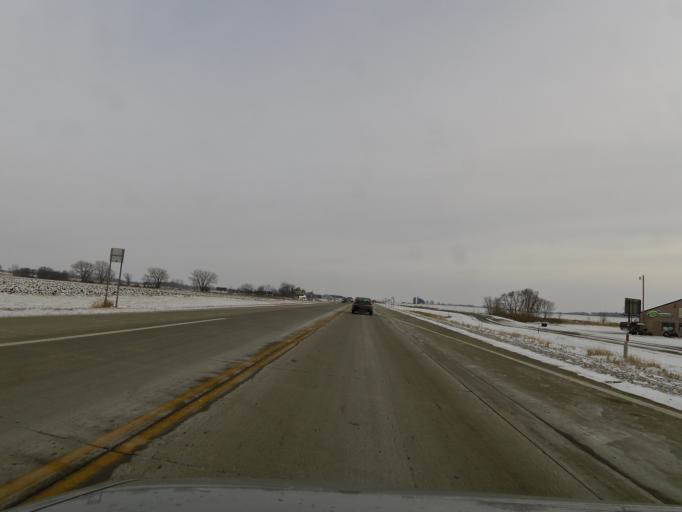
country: US
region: Minnesota
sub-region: McLeod County
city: Hutchinson
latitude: 44.8952
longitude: -94.3233
